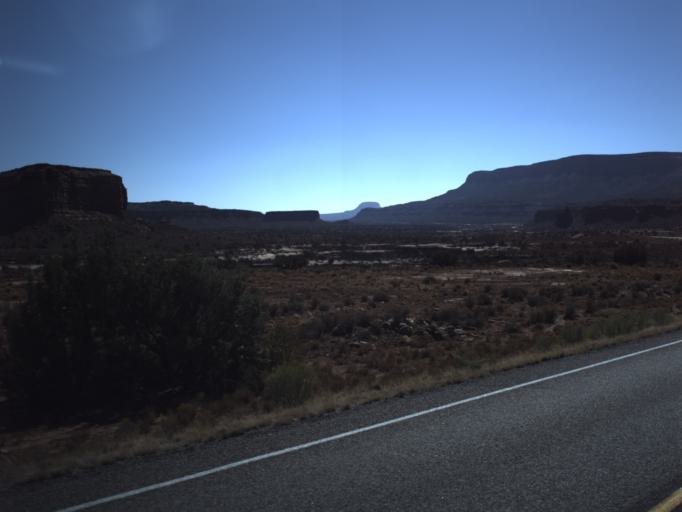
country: US
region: Utah
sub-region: San Juan County
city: Blanding
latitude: 37.7181
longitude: -110.2463
